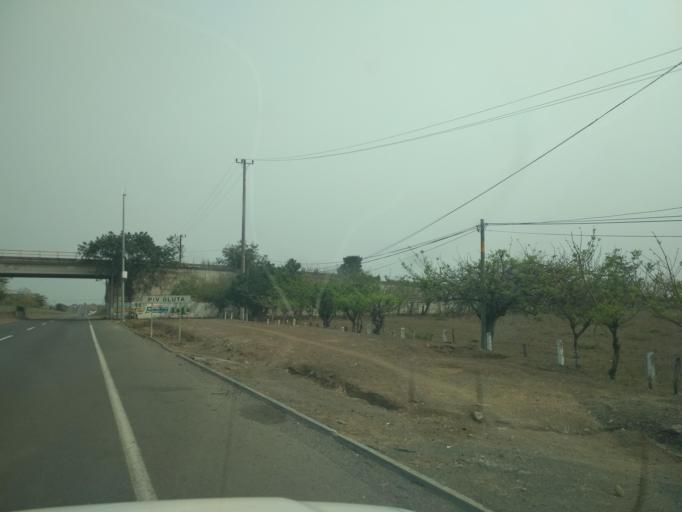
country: MX
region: Veracruz
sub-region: Veracruz
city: Delfino Victoria (Santa Fe)
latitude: 19.1749
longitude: -96.2691
